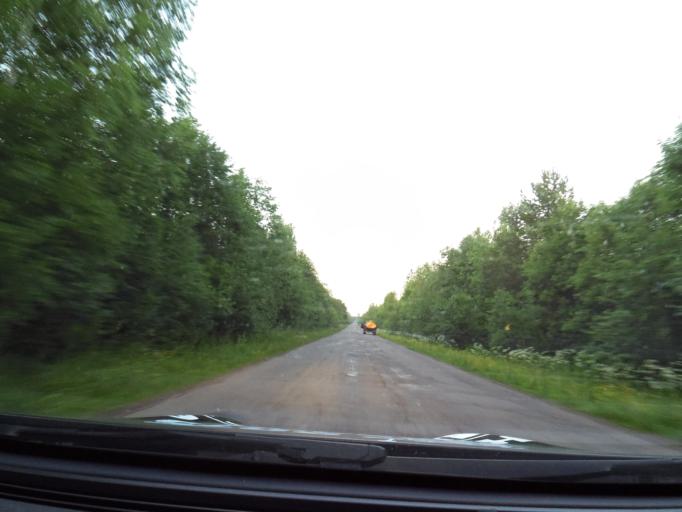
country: RU
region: Leningrad
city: Voznesen'ye
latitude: 60.8279
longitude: 35.7101
